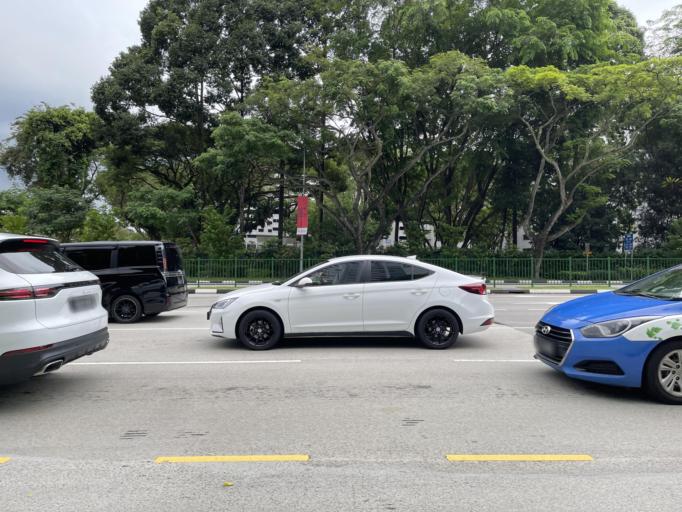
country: SG
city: Singapore
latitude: 1.3115
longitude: 103.7720
